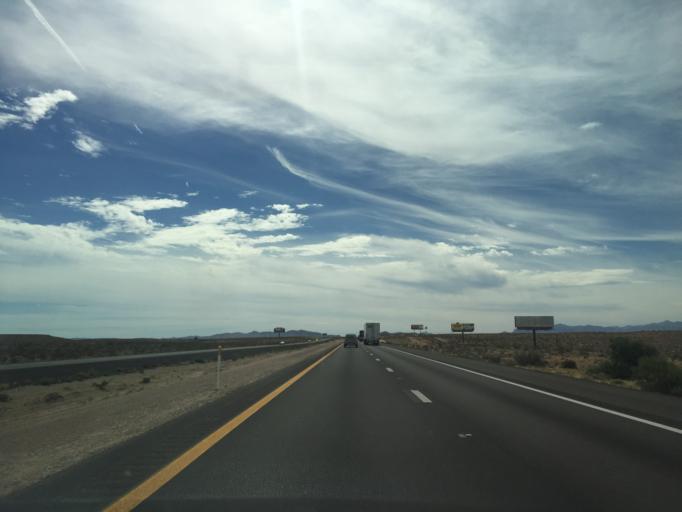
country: US
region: Nevada
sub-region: Clark County
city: Moapa Town
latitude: 36.5283
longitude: -114.7277
